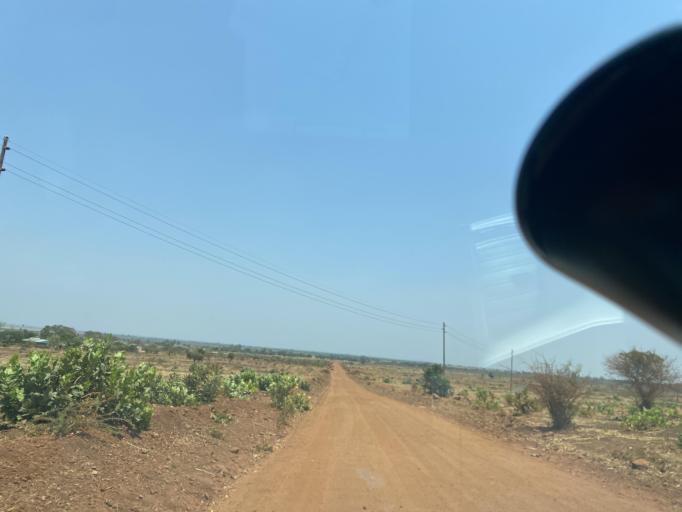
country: ZM
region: Southern
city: Nakambala
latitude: -15.5030
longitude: 27.9266
